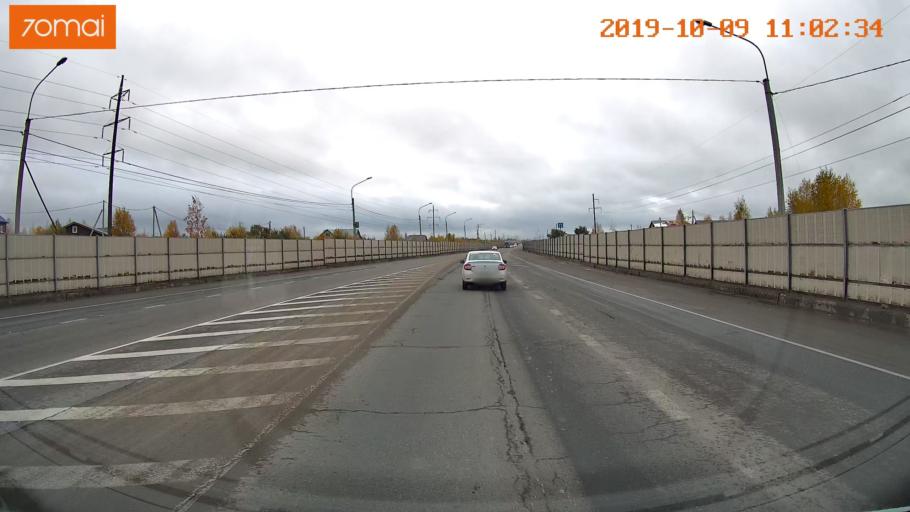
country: RU
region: Vologda
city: Vologda
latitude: 59.2302
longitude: 39.7746
